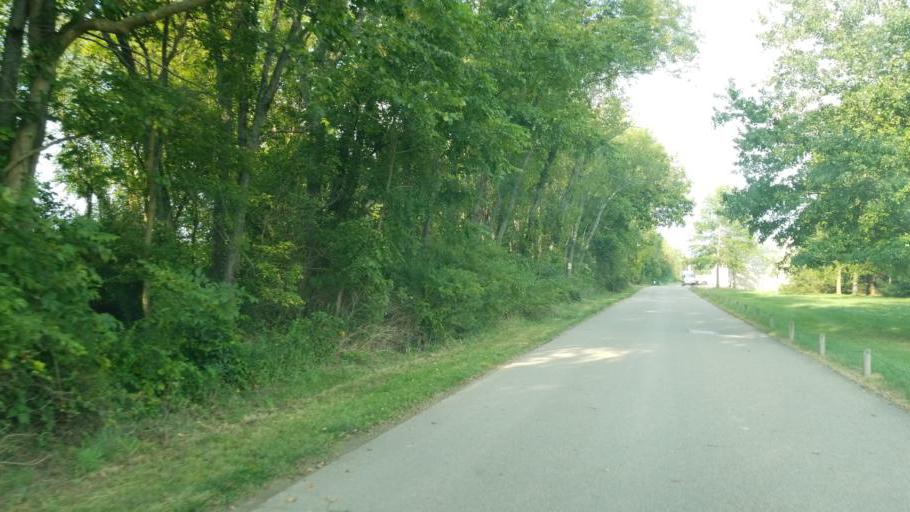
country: US
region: Ohio
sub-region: Knox County
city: Gambier
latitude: 40.3703
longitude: -82.3895
